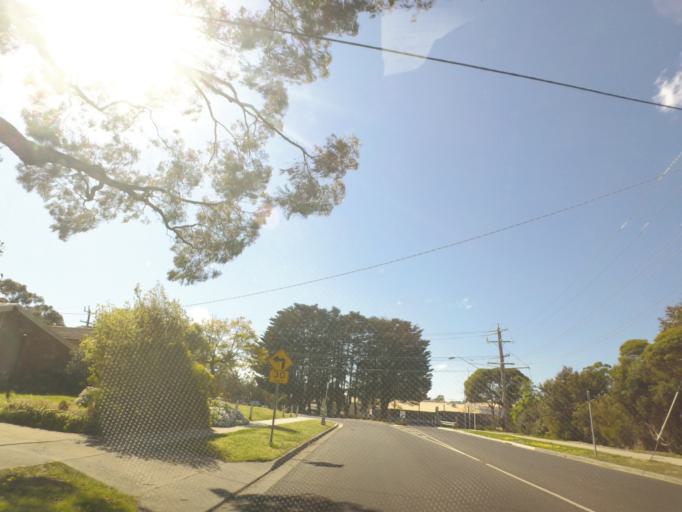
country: AU
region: Victoria
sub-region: Knox
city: Wantirna
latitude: -37.8571
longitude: 145.2287
